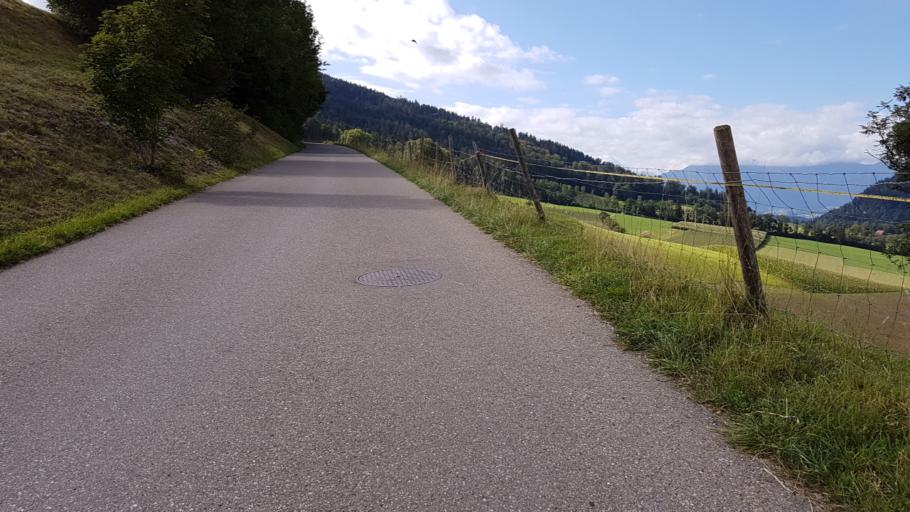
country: CH
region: Bern
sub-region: Bern-Mittelland District
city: Konolfingen
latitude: 46.8673
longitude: 7.6320
